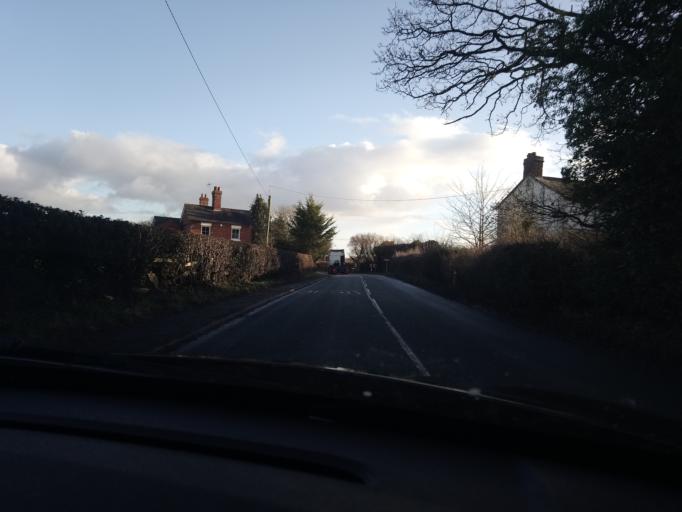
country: GB
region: England
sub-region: Shropshire
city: Ellesmere
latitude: 52.9147
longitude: -2.9143
